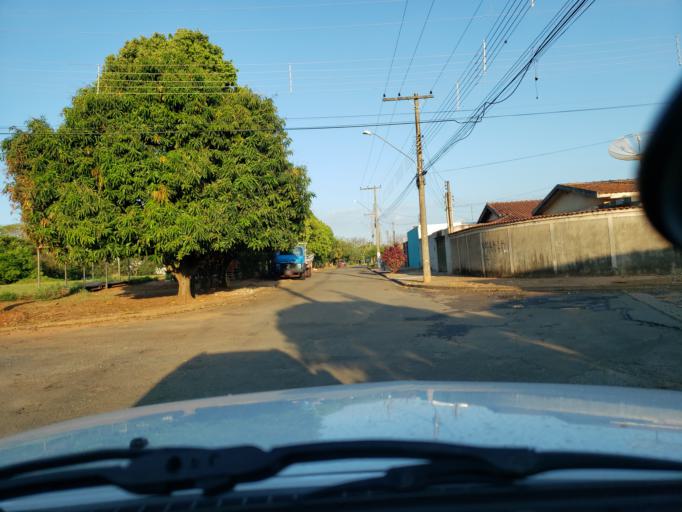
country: BR
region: Sao Paulo
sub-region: Moji-Guacu
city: Mogi-Gaucu
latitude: -22.3413
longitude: -46.9369
